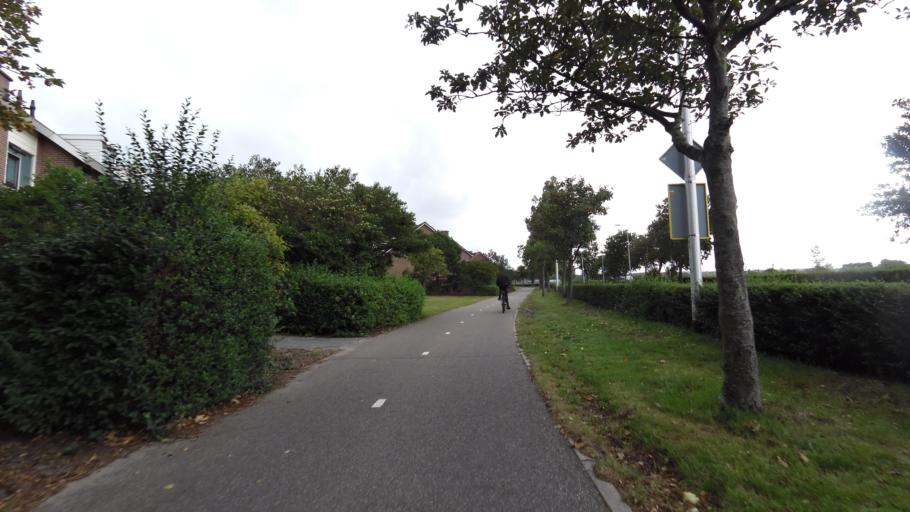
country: NL
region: South Holland
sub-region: Gemeente Noordwijk
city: Noordwijk-Binnen
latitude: 52.2457
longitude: 4.4528
